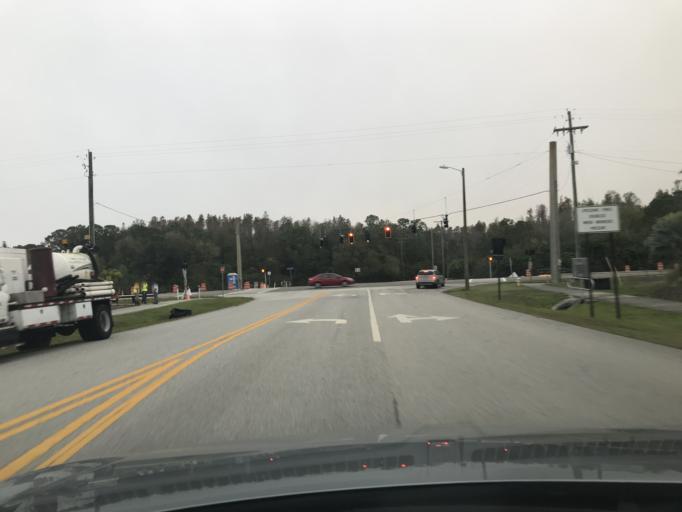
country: US
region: Florida
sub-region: Pinellas County
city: Oldsmar
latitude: 28.0511
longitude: -82.6680
